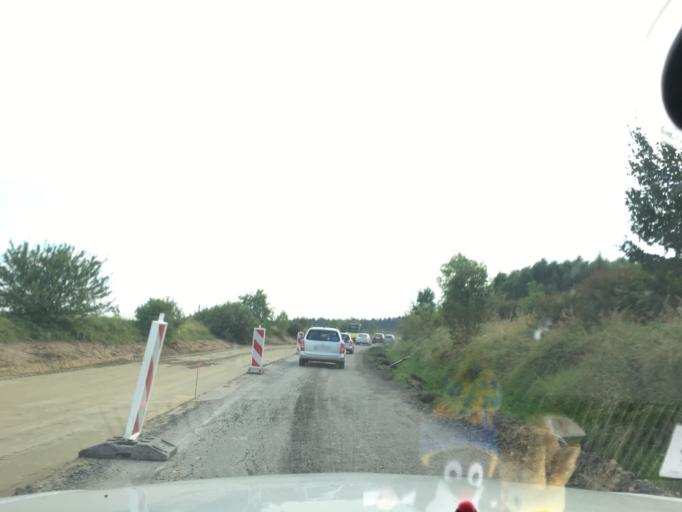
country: PL
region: West Pomeranian Voivodeship
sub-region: Powiat gryficki
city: Rewal
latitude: 54.0700
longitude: 14.9802
